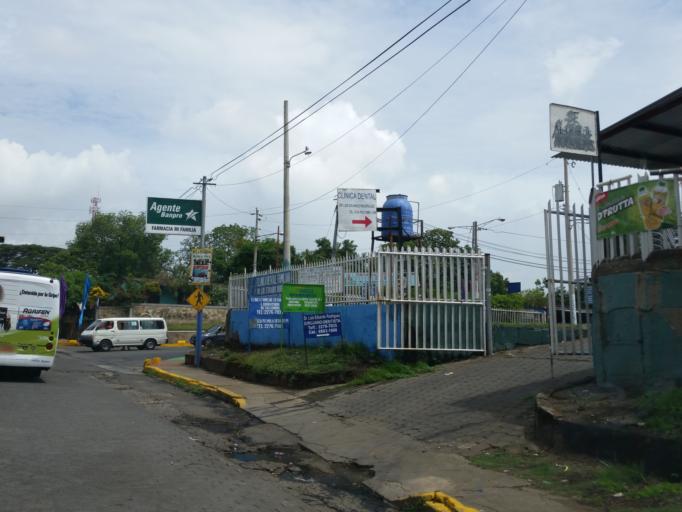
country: NI
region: Masaya
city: Ticuantepe
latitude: 12.0244
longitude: -86.2063
